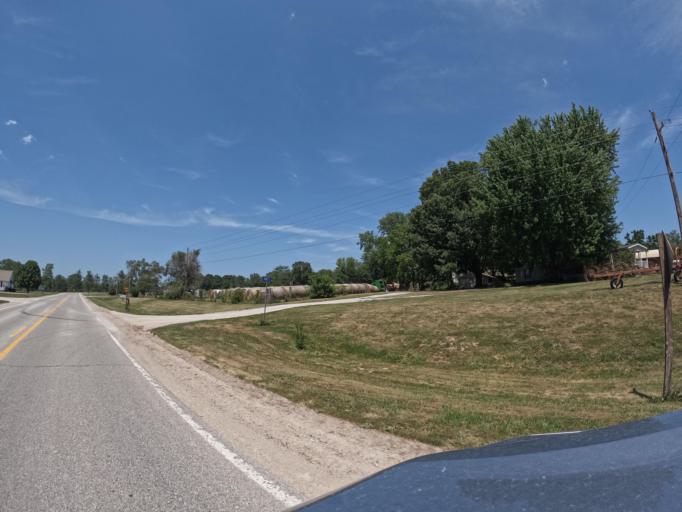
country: US
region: Iowa
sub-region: Henry County
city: Mount Pleasant
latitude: 40.9383
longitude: -91.6144
